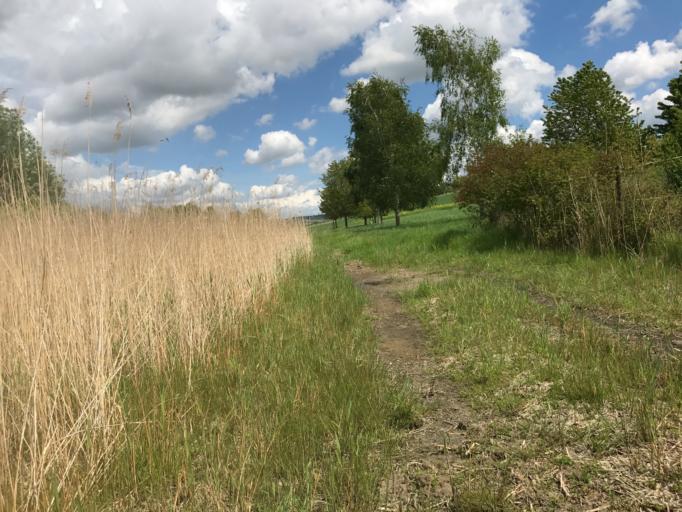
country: DE
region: Rheinland-Pfalz
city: Jugenheim
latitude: 49.8951
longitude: 8.1017
